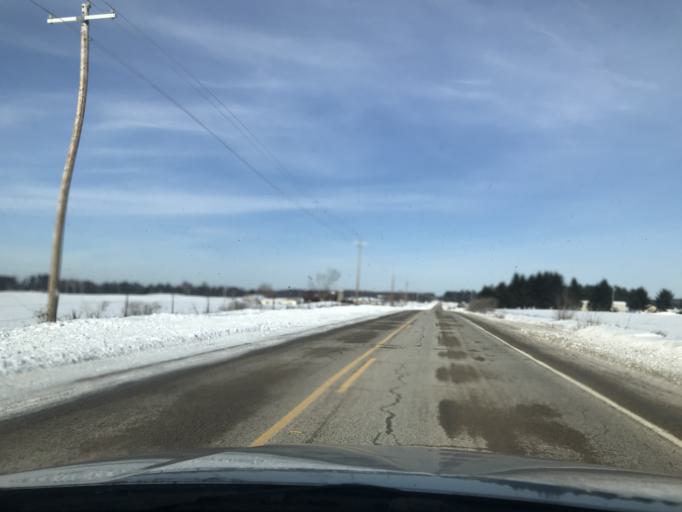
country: US
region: Wisconsin
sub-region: Oconto County
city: Oconto Falls
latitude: 45.1237
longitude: -88.1780
